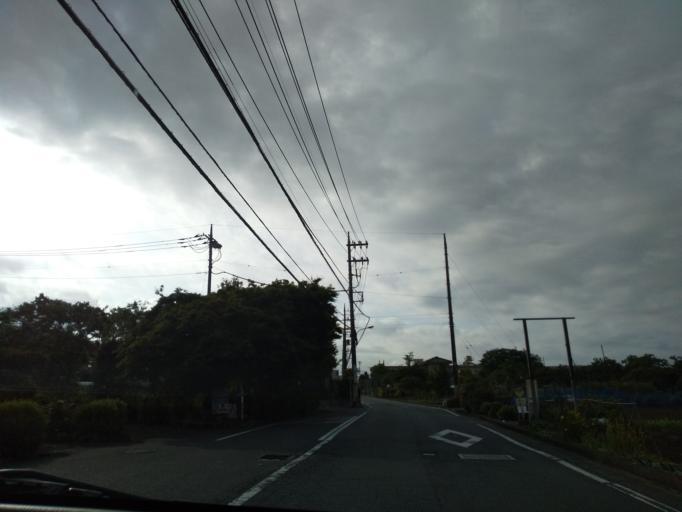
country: JP
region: Tokyo
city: Hachioji
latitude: 35.6895
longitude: 139.3063
